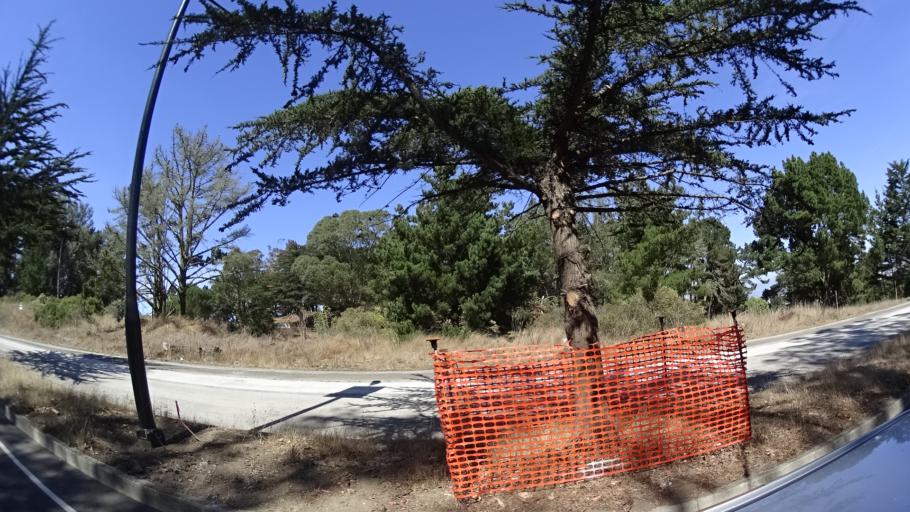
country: US
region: California
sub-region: San Mateo County
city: Brisbane
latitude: 37.7189
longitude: -122.4199
